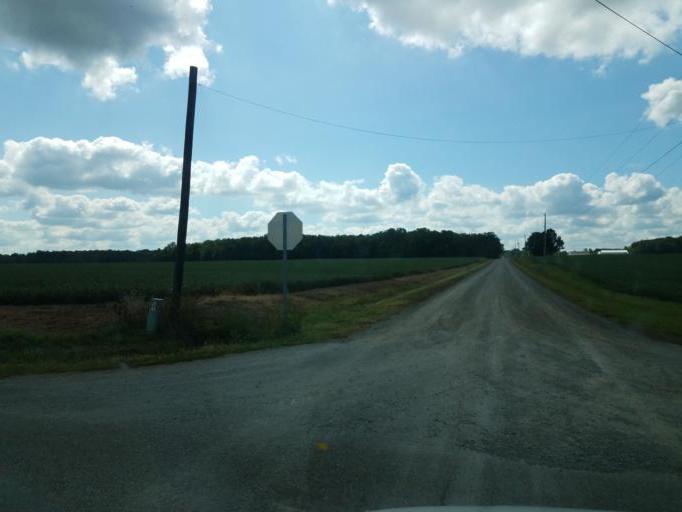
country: US
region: Ohio
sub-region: Wayne County
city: West Salem
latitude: 41.0560
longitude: -82.0961
